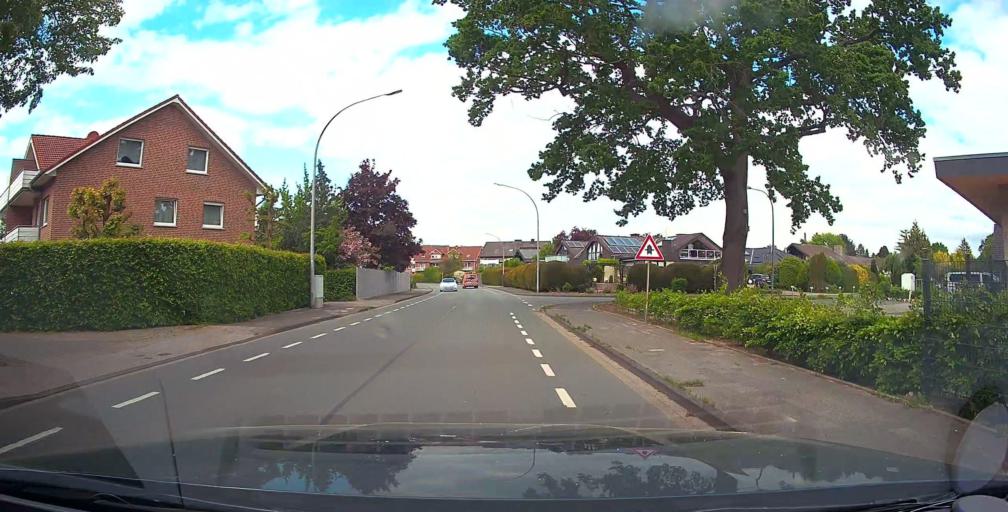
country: DE
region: North Rhine-Westphalia
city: Lengerich
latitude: 52.1824
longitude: 7.8423
